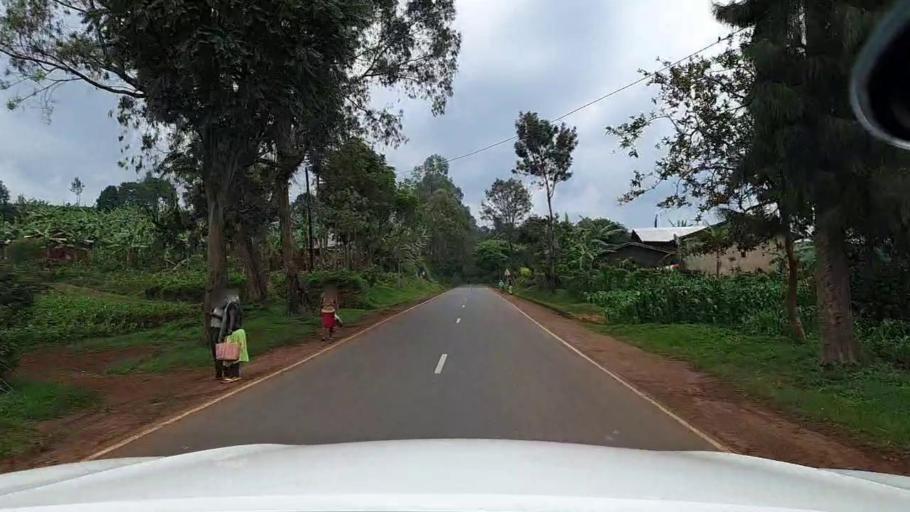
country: RW
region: Western Province
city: Cyangugu
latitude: -2.5383
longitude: 28.8972
